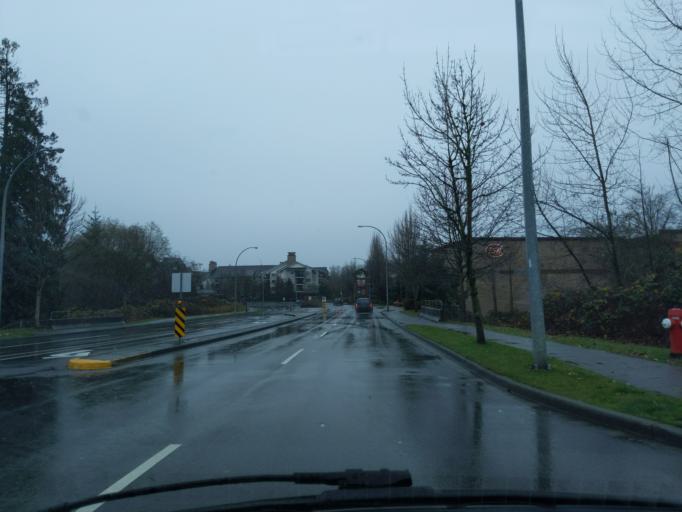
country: CA
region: British Columbia
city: Walnut Grove
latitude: 49.1669
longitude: -122.6627
